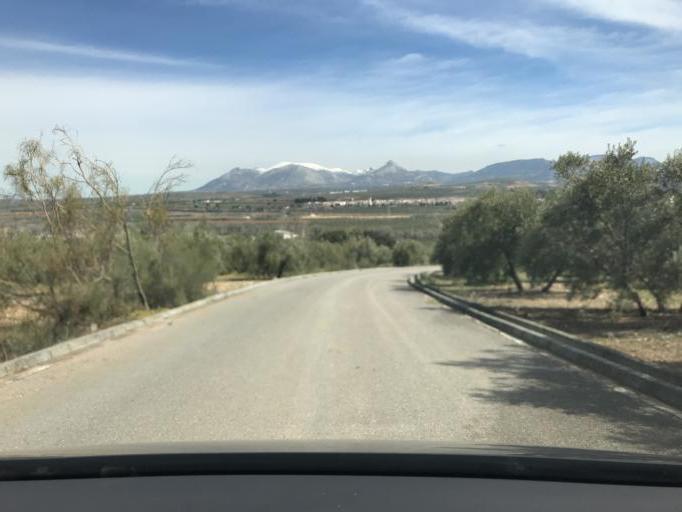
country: ES
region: Andalusia
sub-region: Provincia de Granada
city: Atarfe
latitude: 37.2512
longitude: -3.6764
